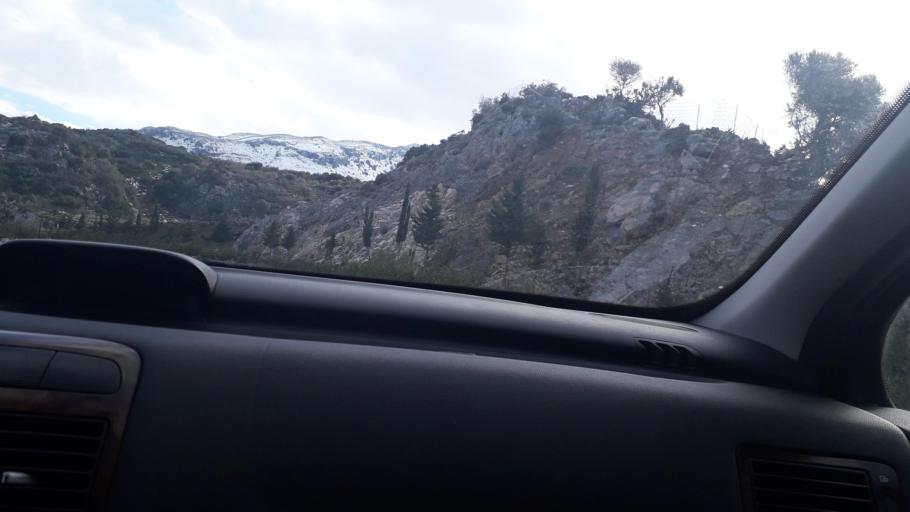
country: GR
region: Crete
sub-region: Nomos Rethymnis
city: Agia Foteini
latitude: 35.2626
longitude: 24.5614
